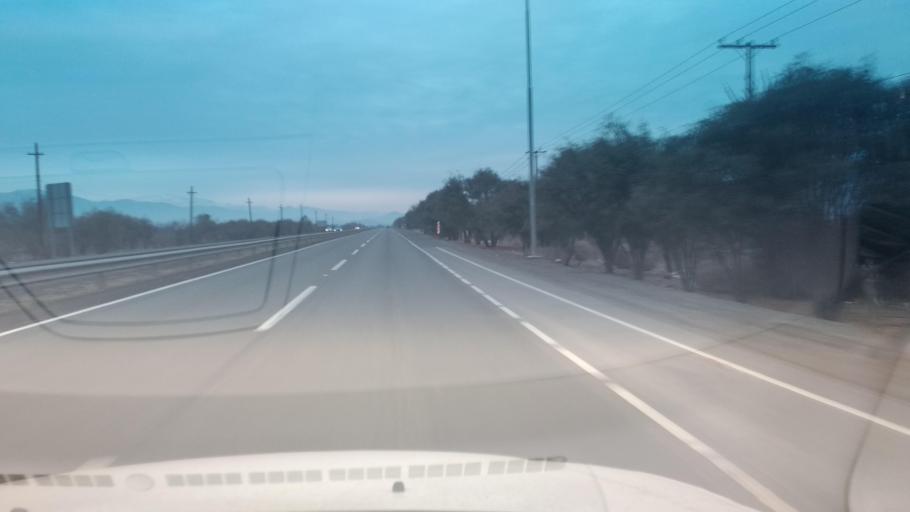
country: CL
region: Santiago Metropolitan
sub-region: Provincia de Chacabuco
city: Chicureo Abajo
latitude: -33.0988
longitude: -70.6918
